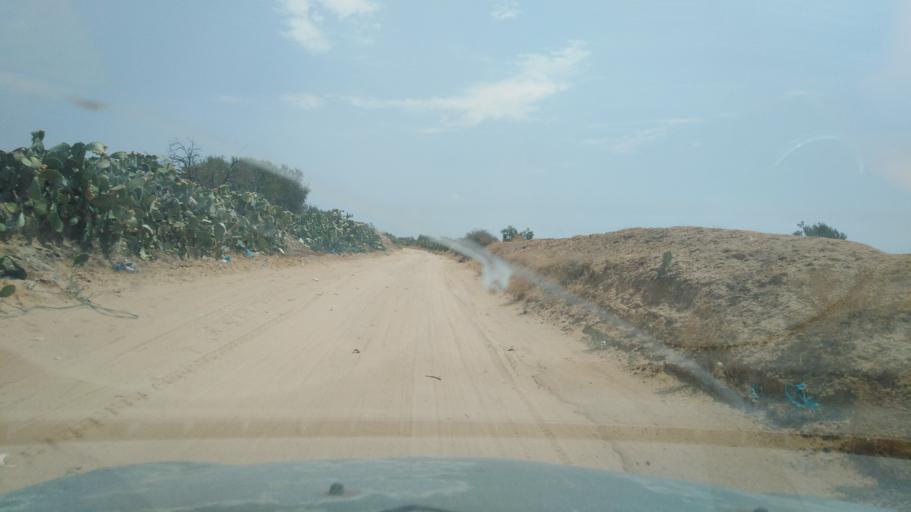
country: TN
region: Safaqis
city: Sfax
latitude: 34.7389
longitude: 10.5487
